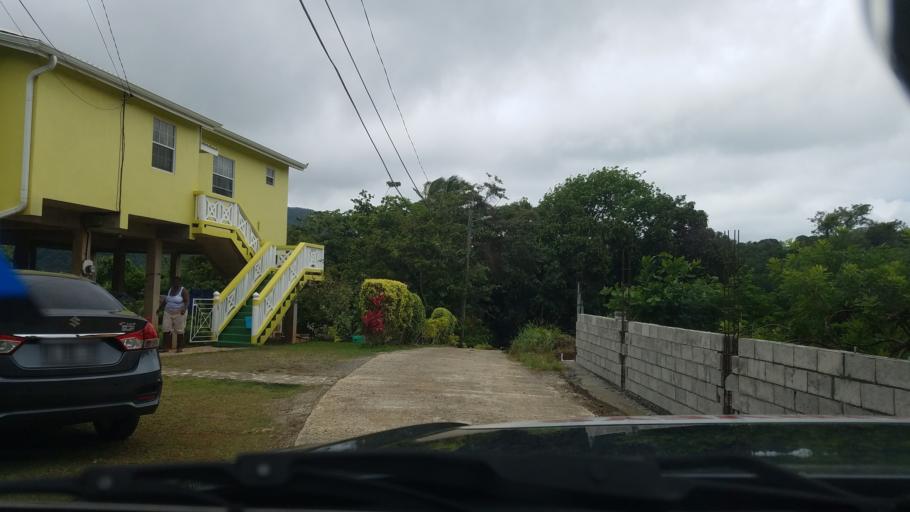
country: LC
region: Castries Quarter
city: Bisee
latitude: 14.0130
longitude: -60.9278
